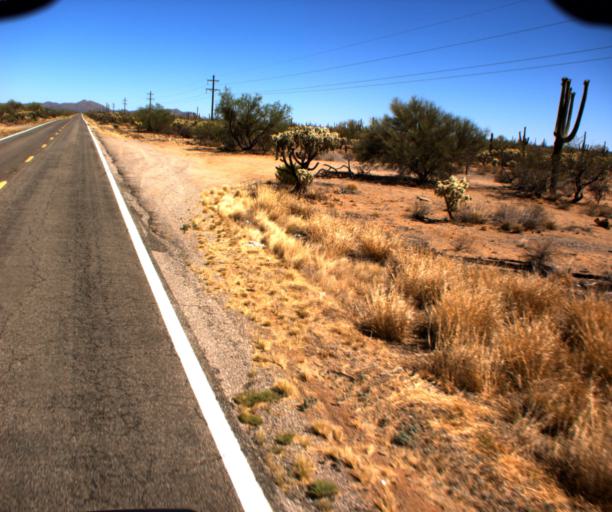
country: US
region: Arizona
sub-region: Pima County
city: Sells
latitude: 32.1083
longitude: -112.0720
